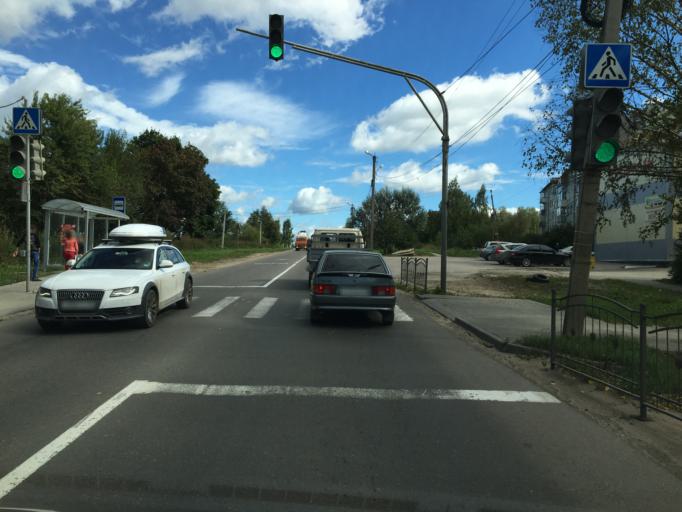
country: RU
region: Kaluga
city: Kaluga
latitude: 54.5457
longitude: 36.3291
